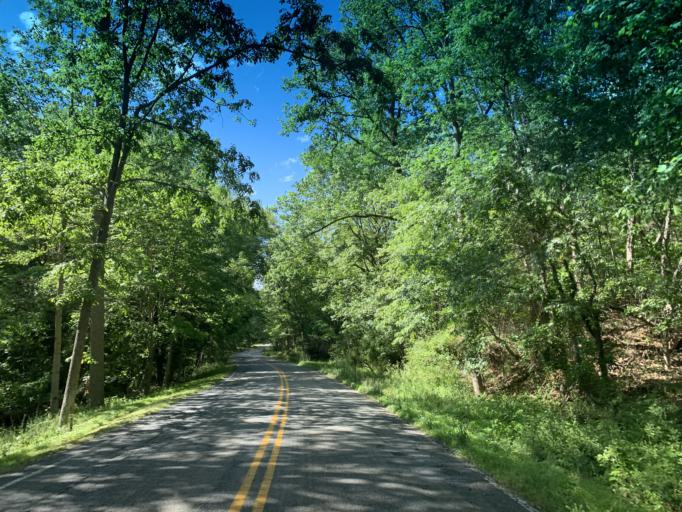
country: US
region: Maryland
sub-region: Cecil County
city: North East
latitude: 39.5513
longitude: -75.9222
